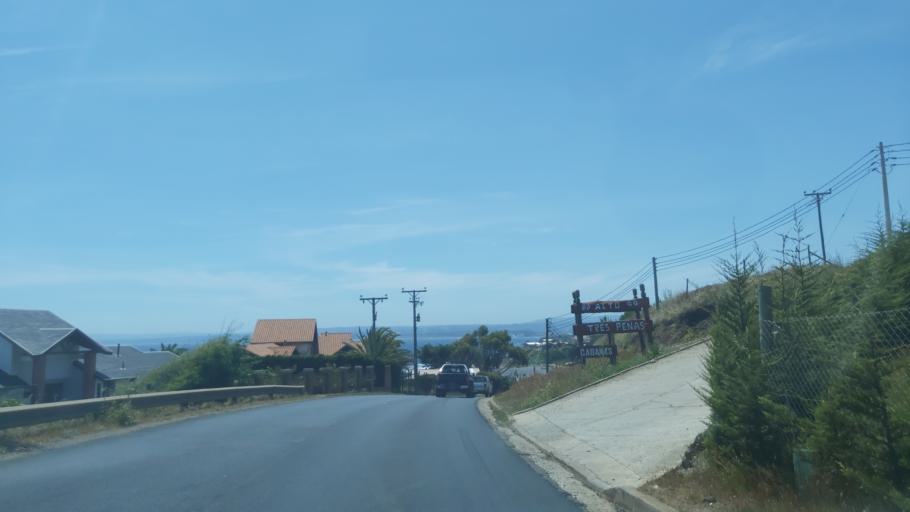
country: CL
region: Maule
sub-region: Provincia de Cauquenes
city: Cauquenes
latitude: -35.8274
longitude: -72.6138
